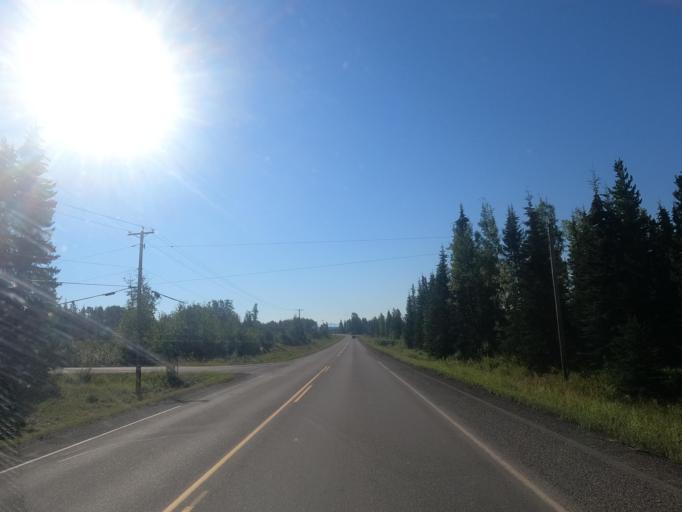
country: CA
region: British Columbia
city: Burns Lake
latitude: 54.3519
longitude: -125.9153
